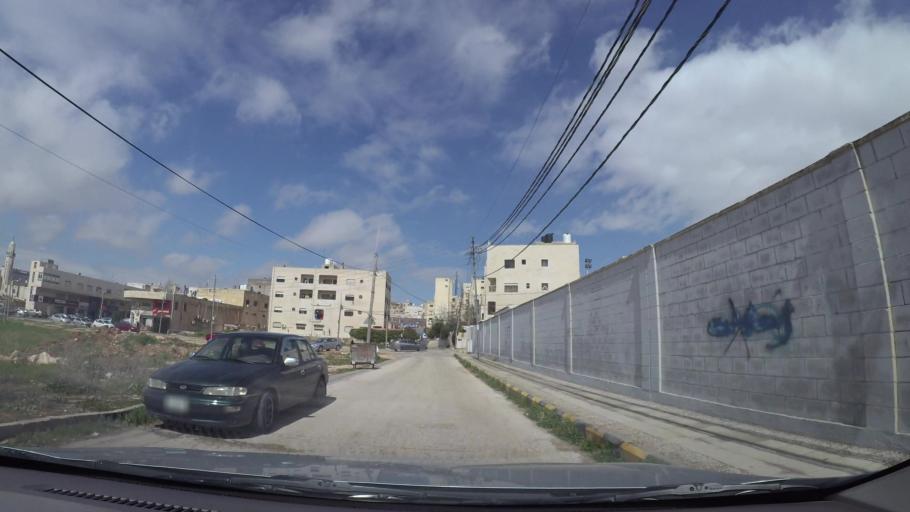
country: JO
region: Amman
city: Al Jubayhah
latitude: 31.9947
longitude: 35.8491
